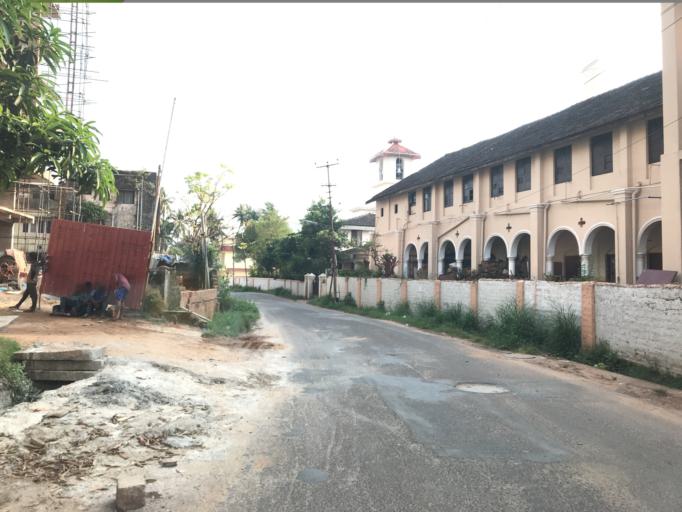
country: IN
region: Karnataka
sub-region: Dakshina Kannada
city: Ullal
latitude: 12.8564
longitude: 74.8368
